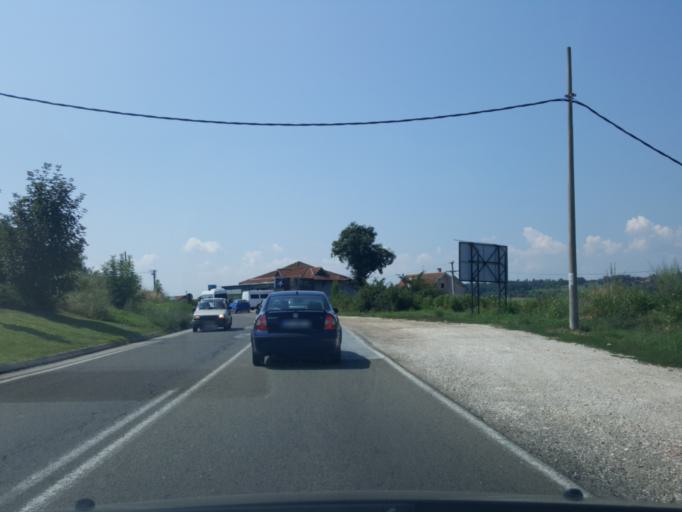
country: RS
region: Central Serbia
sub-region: Belgrade
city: Mladenovac
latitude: 44.4709
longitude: 20.6646
